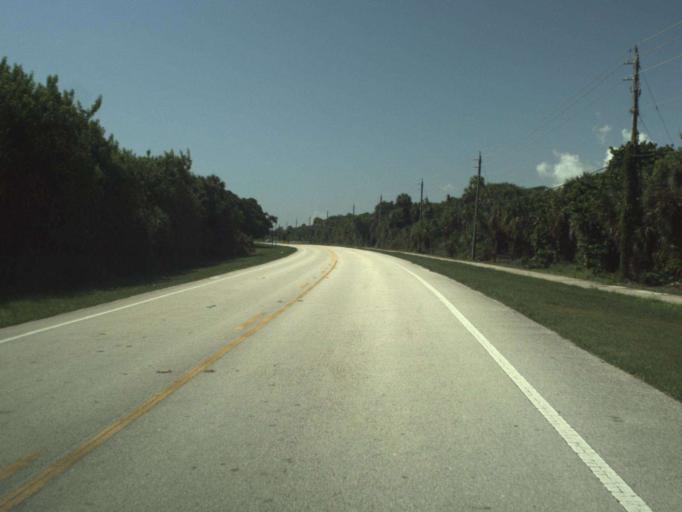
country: US
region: Florida
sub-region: Indian River County
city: Sebastian
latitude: 27.8145
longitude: -80.4259
